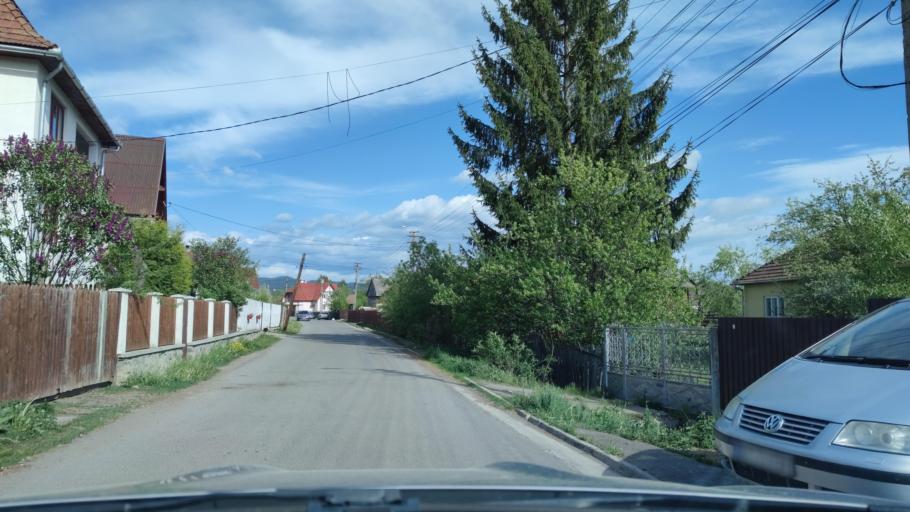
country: RO
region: Harghita
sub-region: Comuna Remetea
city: Remetea
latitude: 46.7999
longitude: 25.4785
